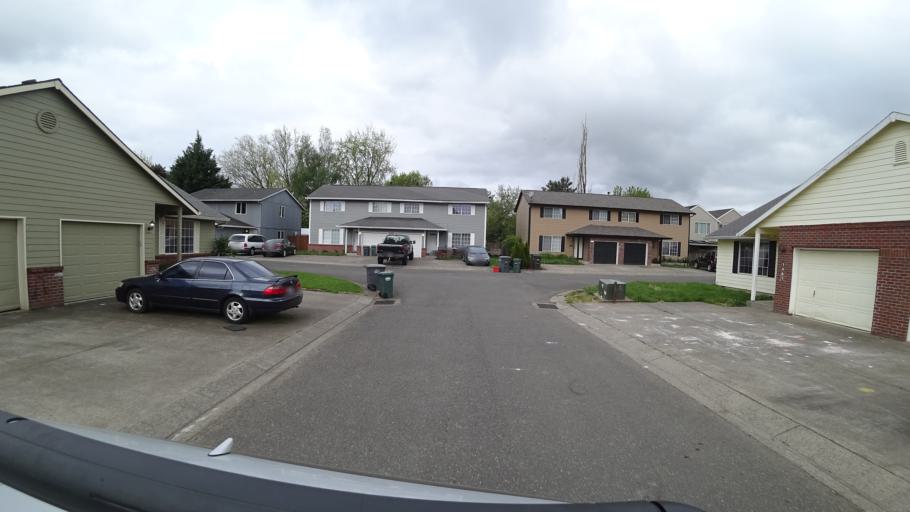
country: US
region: Oregon
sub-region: Washington County
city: Hillsboro
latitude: 45.5373
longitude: -122.9670
